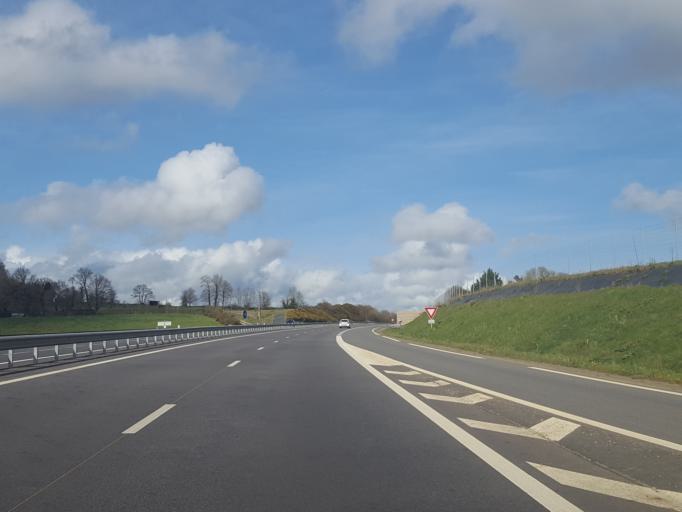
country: FR
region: Brittany
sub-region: Departement d'Ille-et-Vilaine
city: Guichen
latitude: 47.9458
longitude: -1.8260
